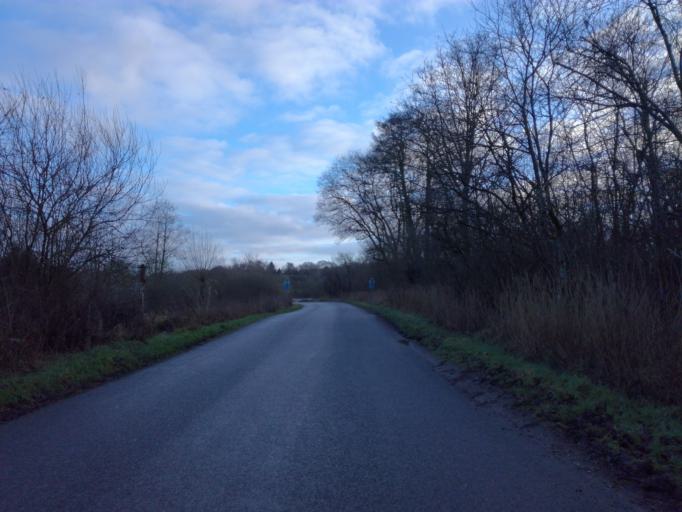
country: DK
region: South Denmark
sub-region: Fredericia Kommune
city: Taulov
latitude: 55.5490
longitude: 9.6017
